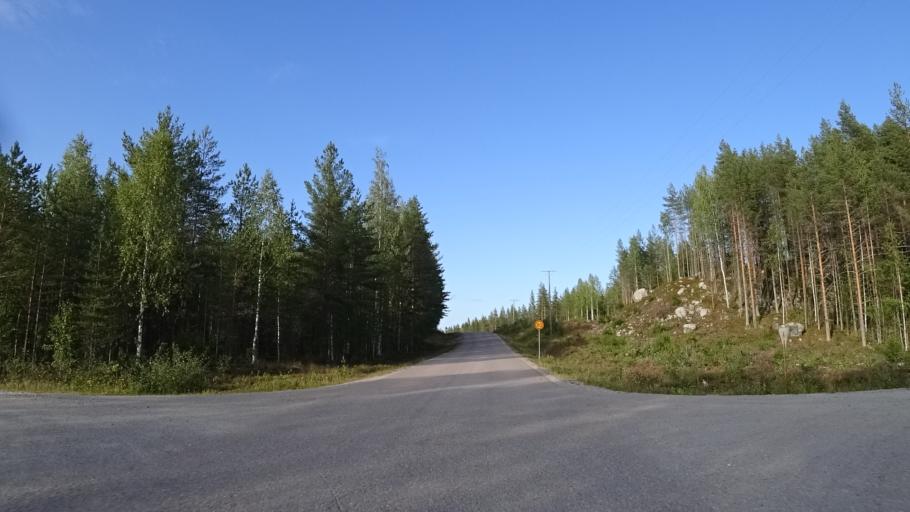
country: FI
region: North Karelia
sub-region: Joensuu
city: Eno
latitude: 63.0645
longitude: 30.5559
